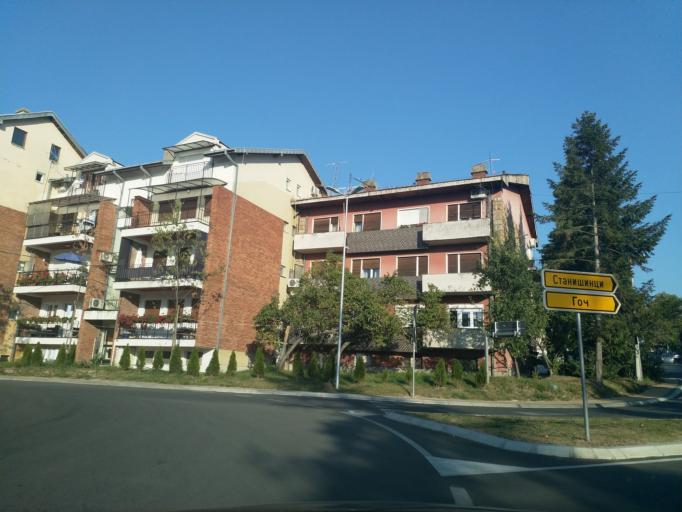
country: RS
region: Central Serbia
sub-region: Raski Okrug
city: Vrnjacka Banja
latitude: 43.6202
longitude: 20.8975
